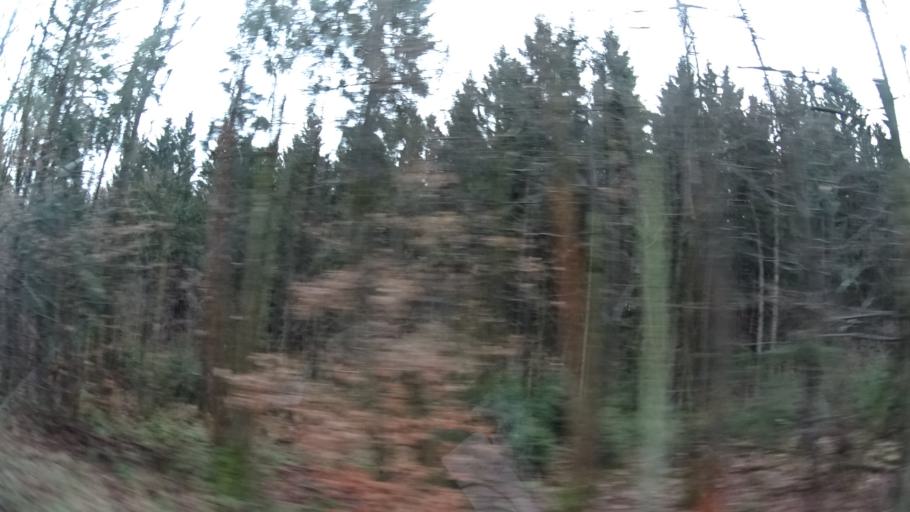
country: DE
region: Hesse
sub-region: Regierungsbezirk Kassel
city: Hilders
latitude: 50.6181
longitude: 9.9767
